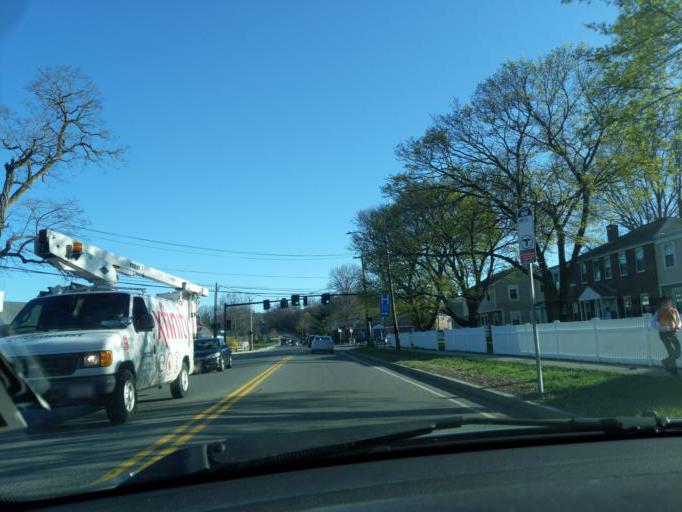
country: US
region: Massachusetts
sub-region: Essex County
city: Beverly
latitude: 42.5627
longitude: -70.8793
